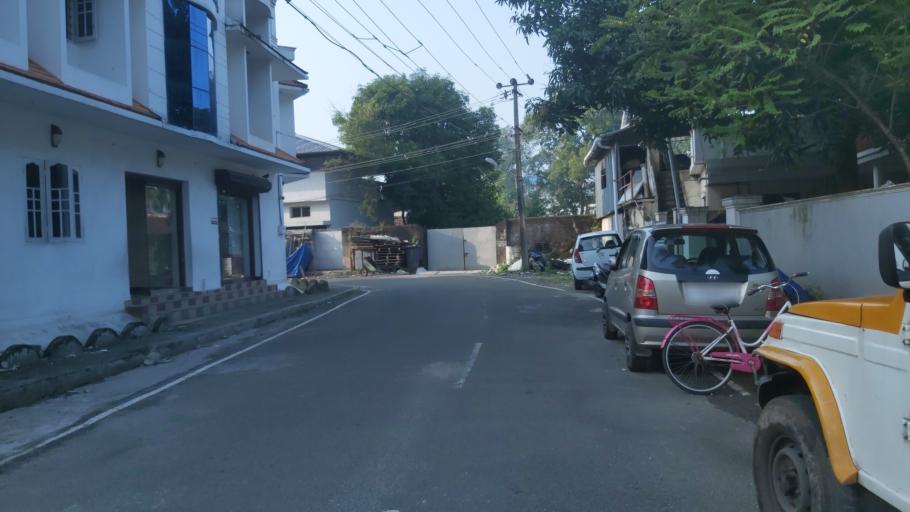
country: IN
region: Kerala
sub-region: Ernakulam
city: Cochin
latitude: 9.9616
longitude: 76.2564
